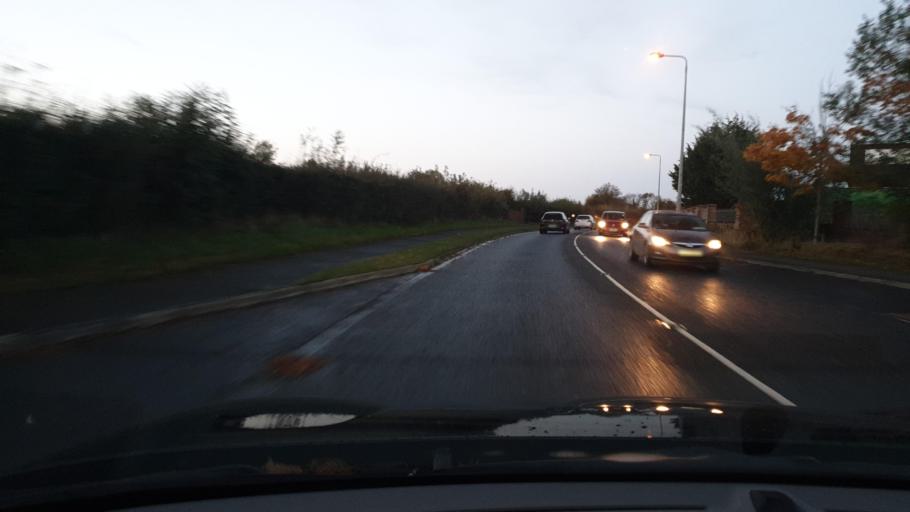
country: IE
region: Leinster
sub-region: An Mhi
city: Ashbourne
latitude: 53.5159
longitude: -6.4185
